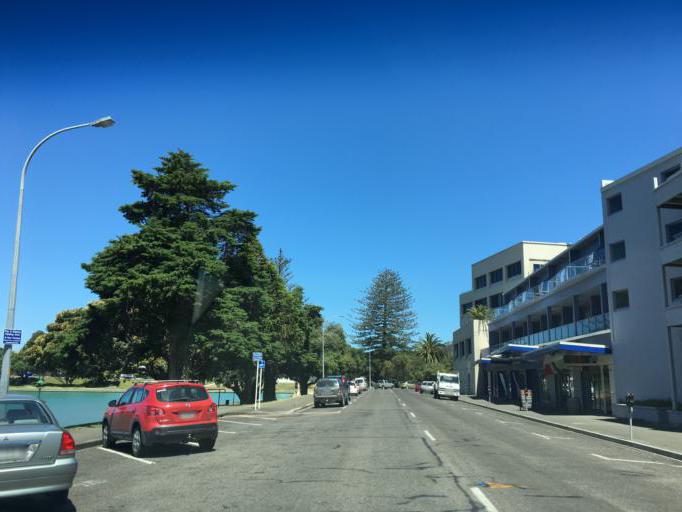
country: NZ
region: Gisborne
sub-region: Gisborne District
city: Gisborne
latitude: -38.6668
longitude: 178.0281
